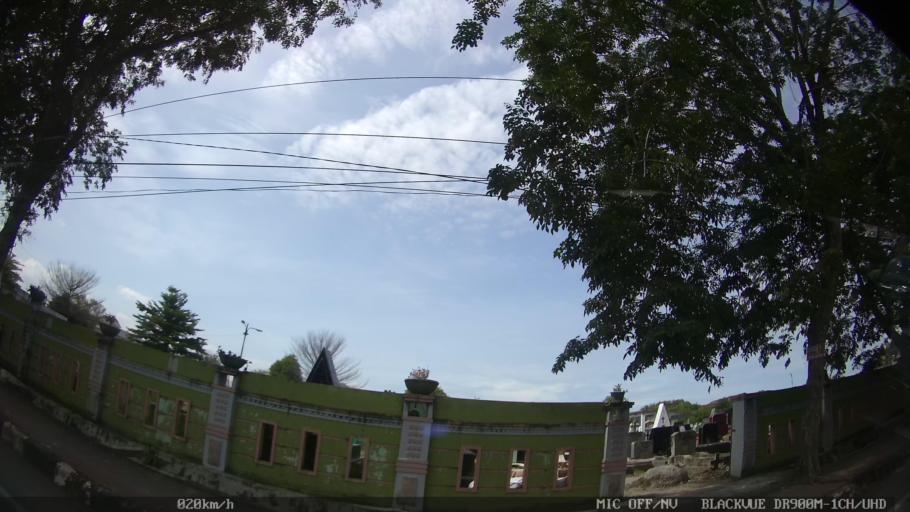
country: ID
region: North Sumatra
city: Medan
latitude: 3.5847
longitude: 98.6570
